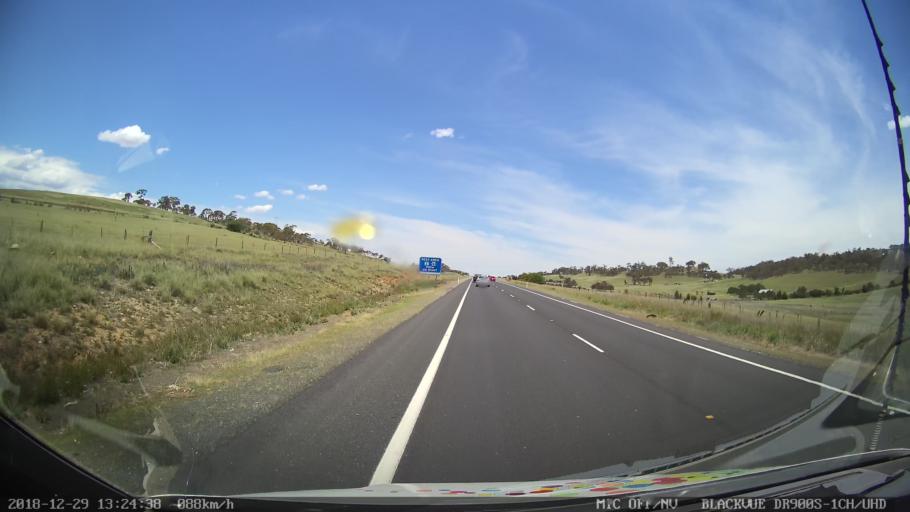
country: AU
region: New South Wales
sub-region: Cooma-Monaro
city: Cooma
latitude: -35.8322
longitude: 149.1623
